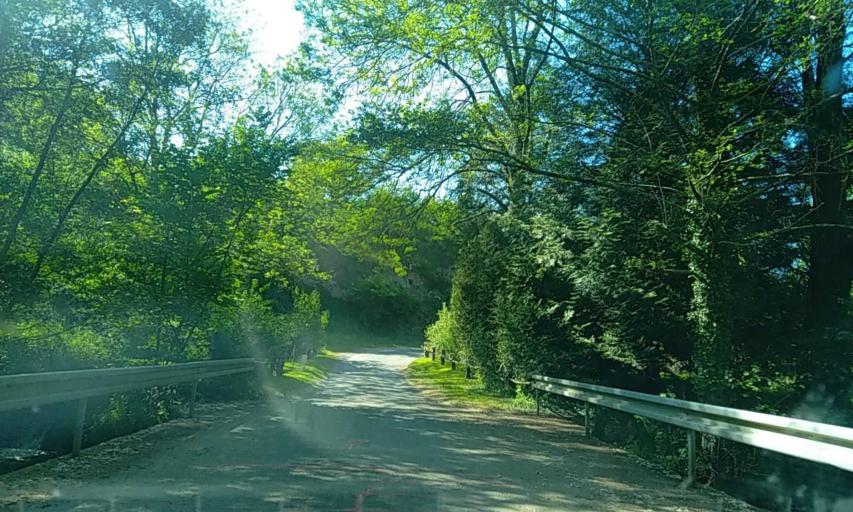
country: FR
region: Poitou-Charentes
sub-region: Departement des Deux-Sevres
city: Chiche
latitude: 46.7879
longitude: -0.3894
